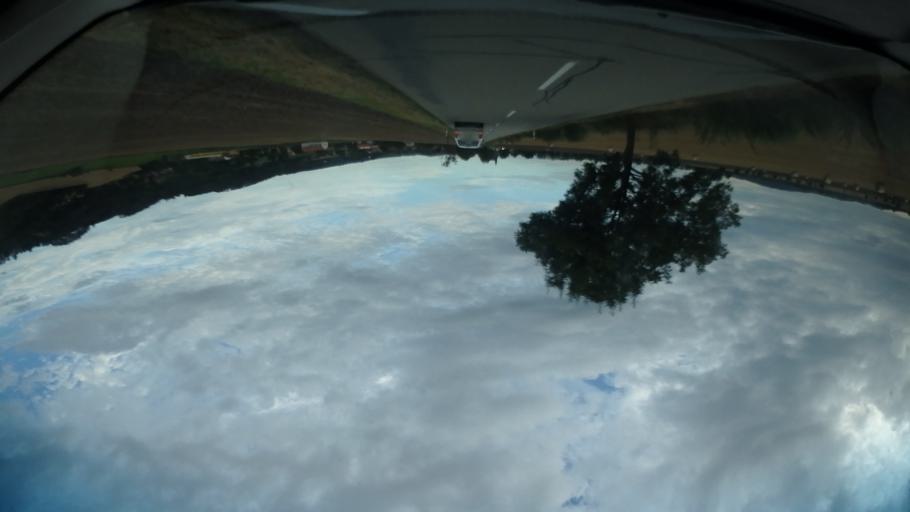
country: CZ
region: South Moravian
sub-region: Okres Blansko
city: Boskovice
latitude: 49.5257
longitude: 16.6835
